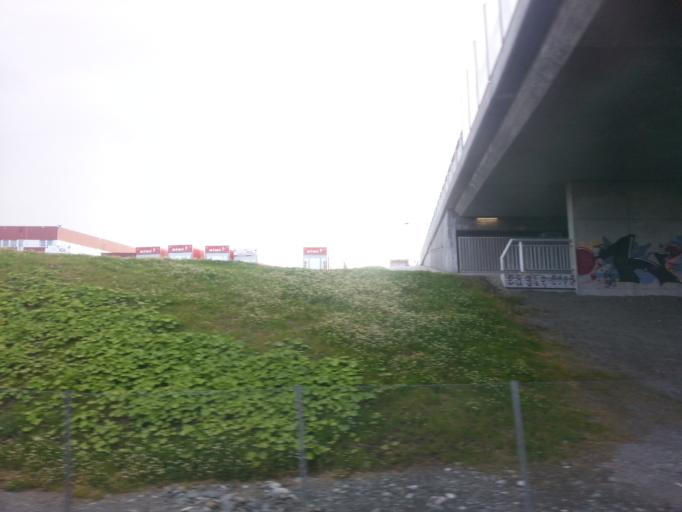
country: NO
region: Sor-Trondelag
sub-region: Trondheim
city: Trondheim
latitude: 63.4378
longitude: 10.4611
